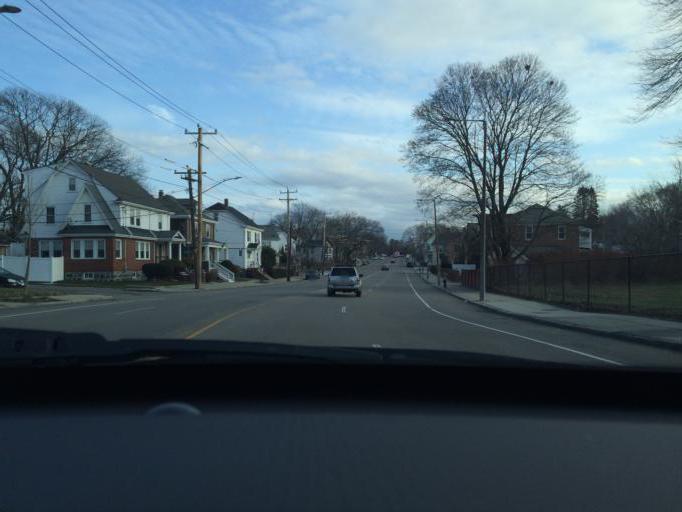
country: US
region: Massachusetts
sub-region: Norfolk County
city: Milton
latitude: 42.2759
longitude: -71.0739
